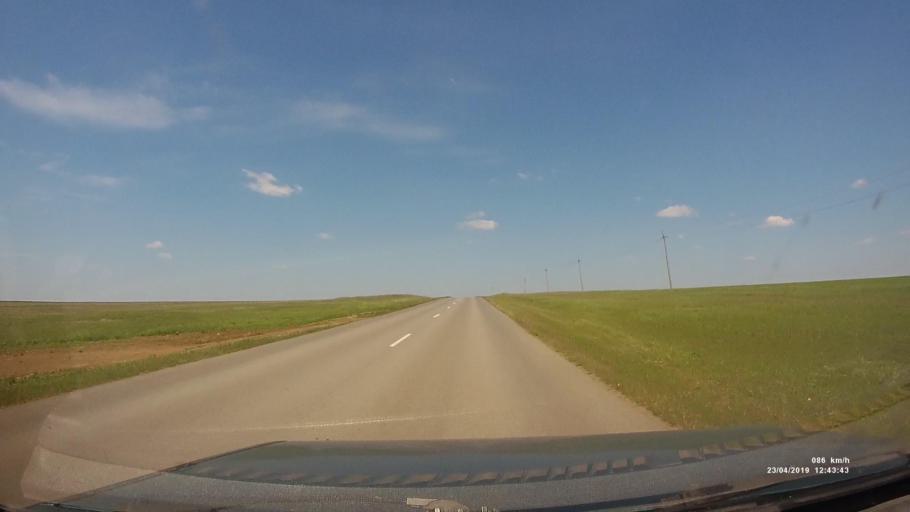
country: RU
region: Kalmykiya
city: Yashalta
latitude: 46.4676
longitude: 42.6501
